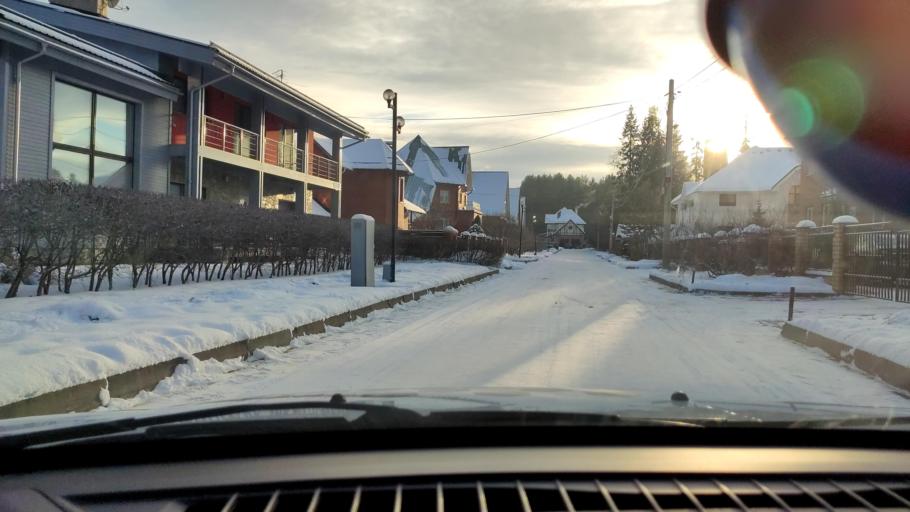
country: RU
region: Perm
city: Kondratovo
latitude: 58.0518
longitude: 56.1014
